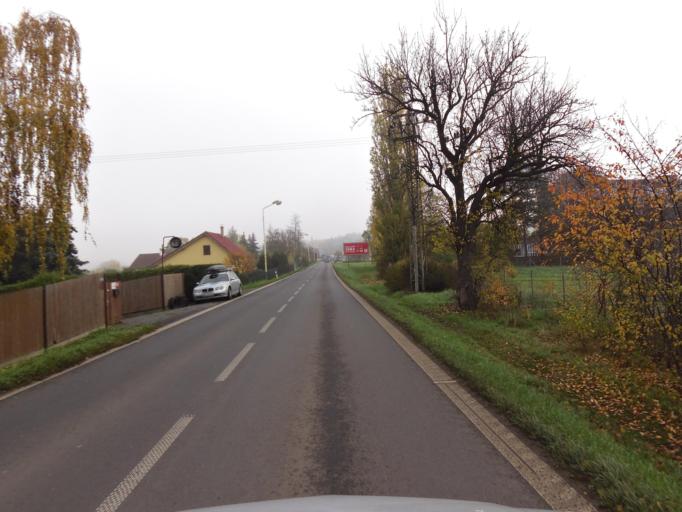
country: CZ
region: Ustecky
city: Zatec
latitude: 50.3240
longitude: 13.5240
